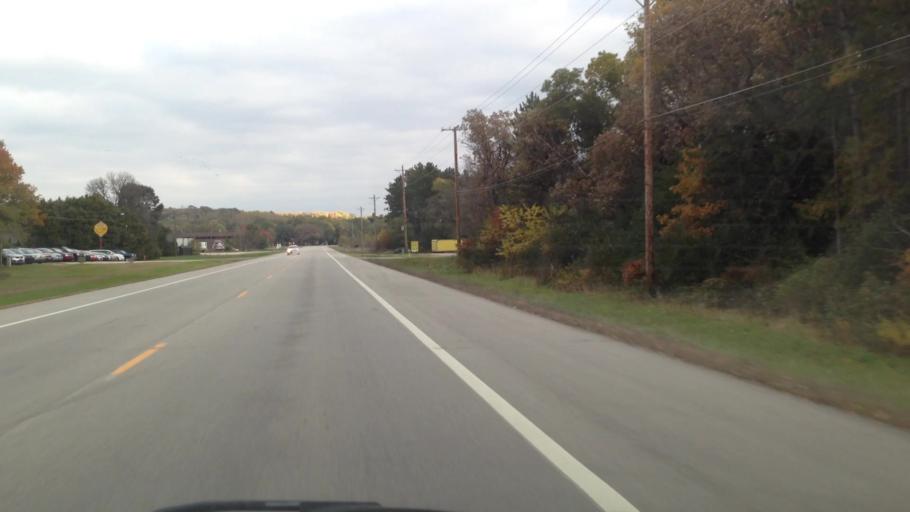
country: US
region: Minnesota
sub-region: Olmsted County
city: Rochester
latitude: 43.9878
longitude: -92.4109
